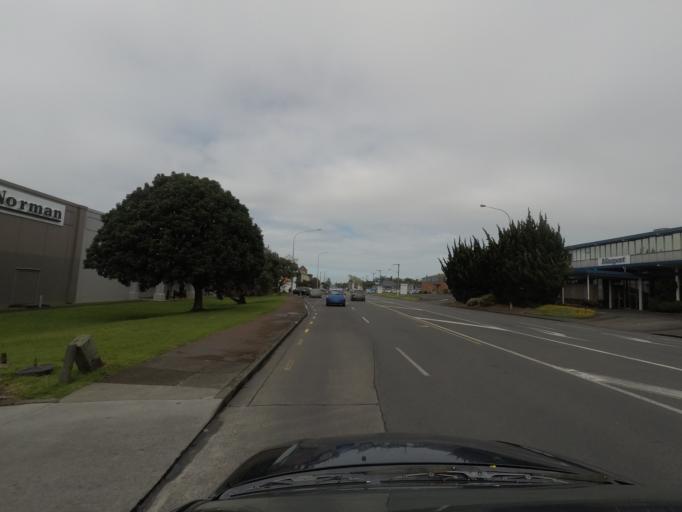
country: NZ
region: Auckland
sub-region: Auckland
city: Tamaki
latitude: -36.8984
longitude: 174.8450
